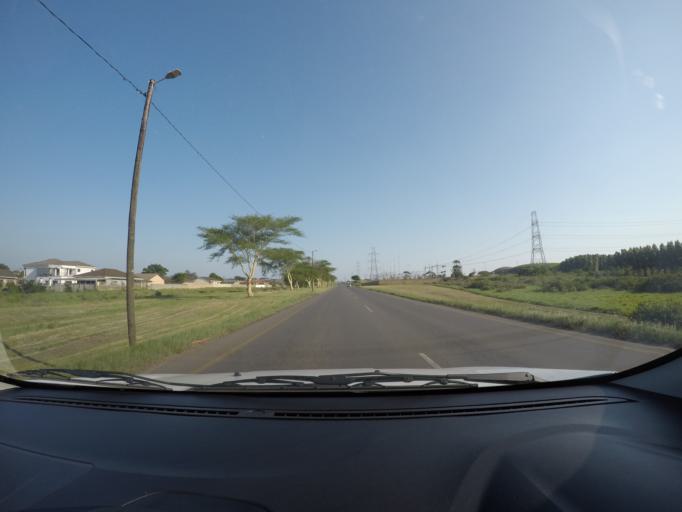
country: ZA
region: KwaZulu-Natal
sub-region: uThungulu District Municipality
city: Richards Bay
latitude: -28.7222
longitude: 32.0340
